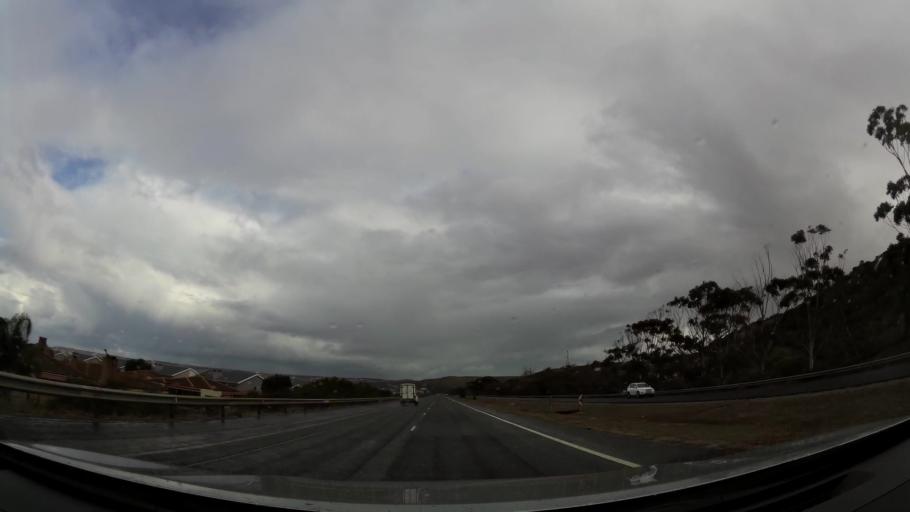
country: ZA
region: Western Cape
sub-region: Eden District Municipality
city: Mossel Bay
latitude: -34.1335
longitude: 22.1019
